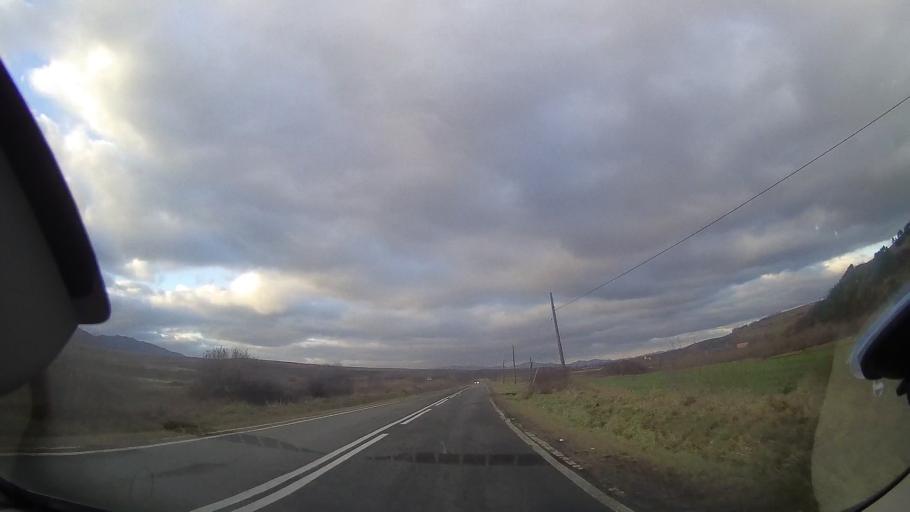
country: RO
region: Cluj
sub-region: Comuna Calatele
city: Calatele
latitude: 46.7873
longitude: 22.9999
